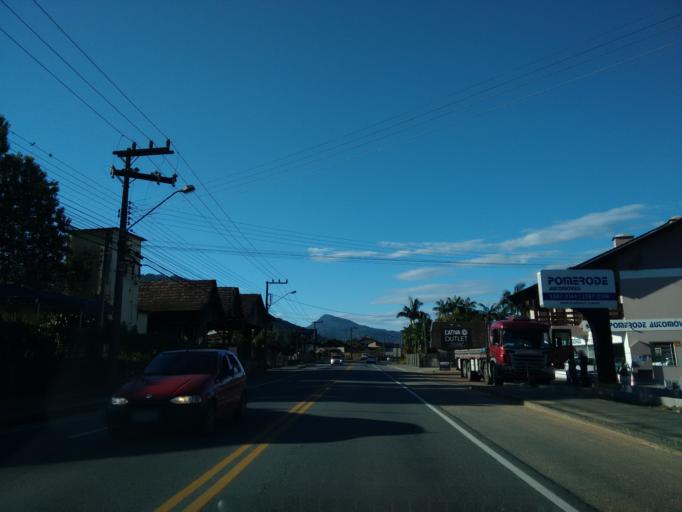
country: BR
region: Santa Catarina
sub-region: Pomerode
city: Pomerode
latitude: -26.7598
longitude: -49.1709
